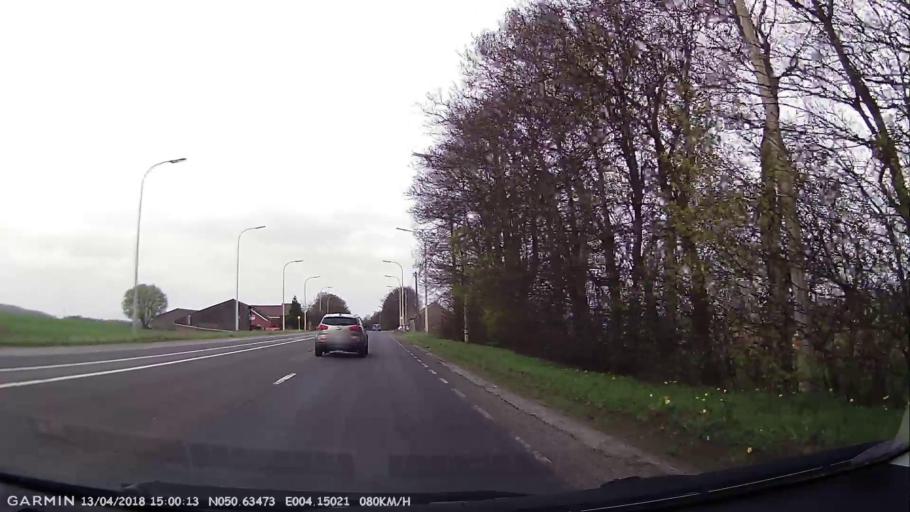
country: BE
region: Wallonia
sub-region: Province du Hainaut
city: Braine-le-Comte
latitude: 50.6349
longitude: 4.1504
